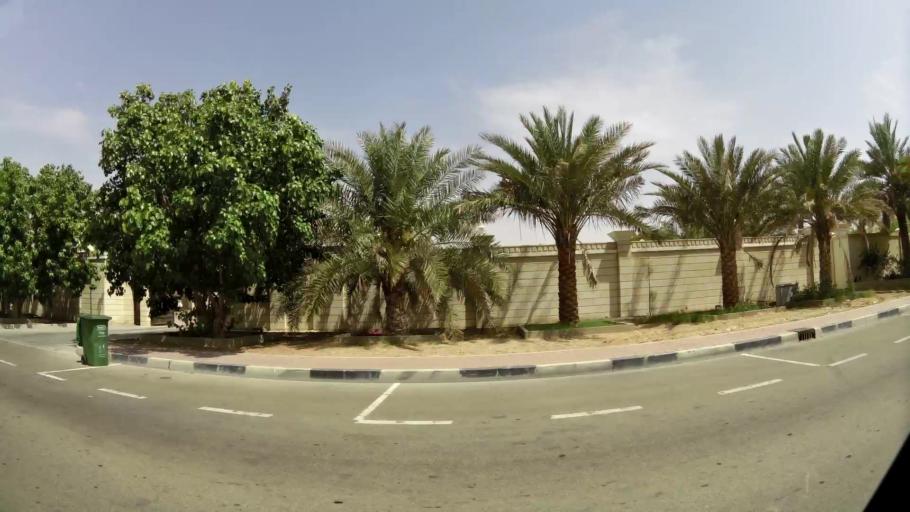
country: AE
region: Abu Dhabi
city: Al Ain
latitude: 24.1761
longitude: 55.7129
